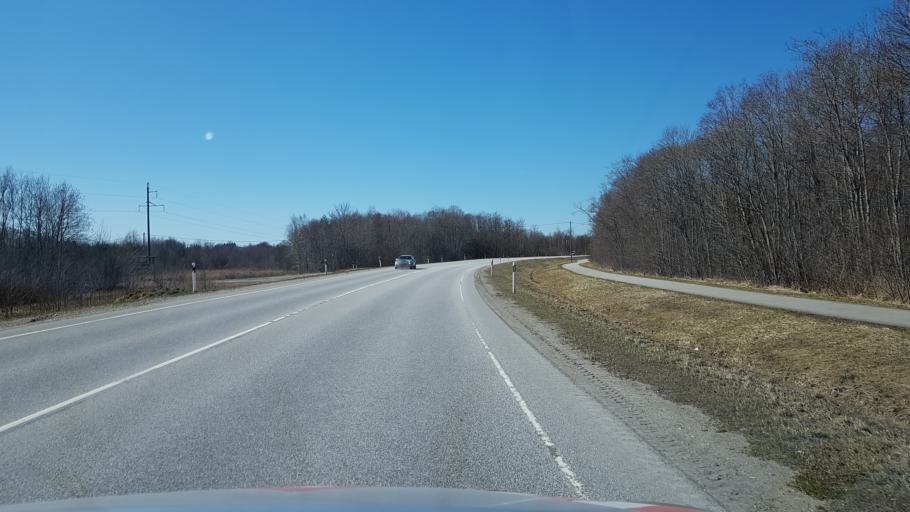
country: EE
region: Laeaene
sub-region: Ridala Parish
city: Uuemoisa
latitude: 58.9500
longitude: 23.6538
